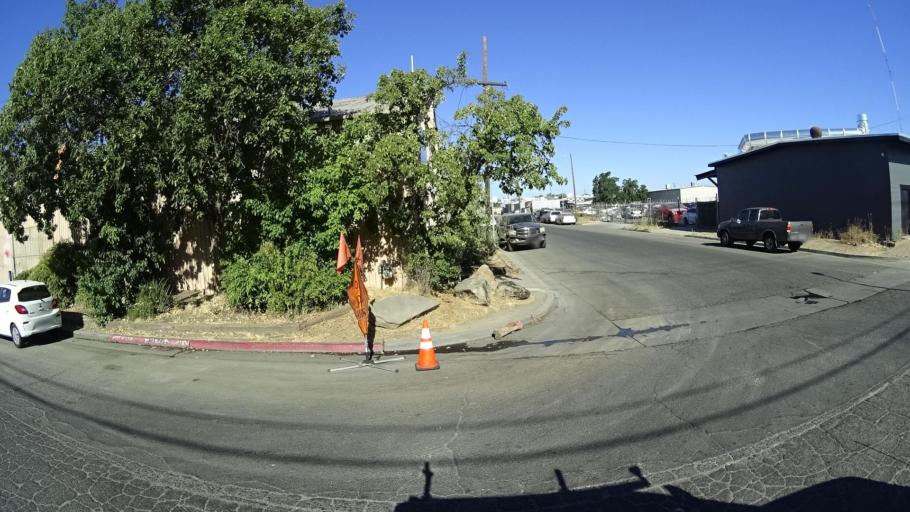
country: US
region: California
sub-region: Fresno County
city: Fresno
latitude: 36.7630
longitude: -119.7861
